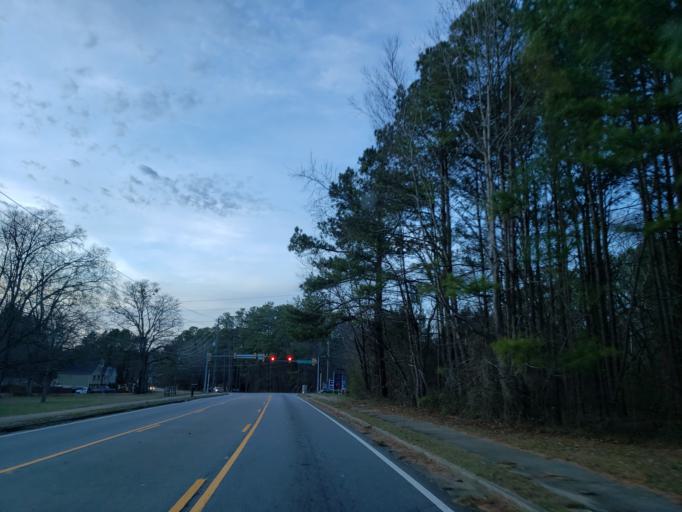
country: US
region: Georgia
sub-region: Cobb County
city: Acworth
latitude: 34.0722
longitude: -84.6338
